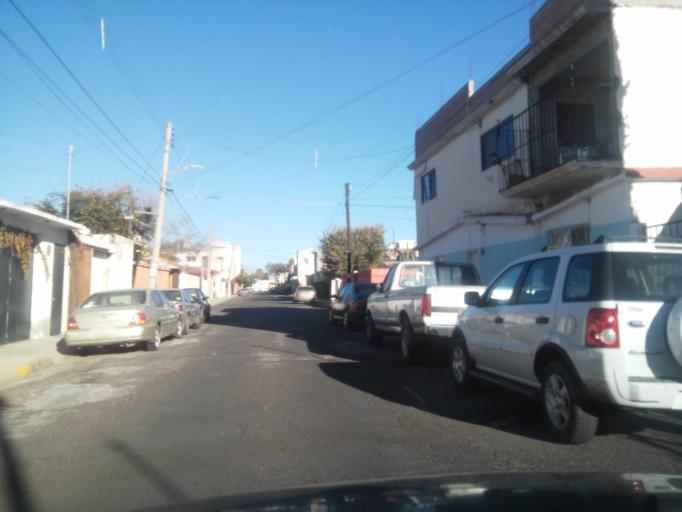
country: MX
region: Durango
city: Victoria de Durango
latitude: 24.0314
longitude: -104.6510
